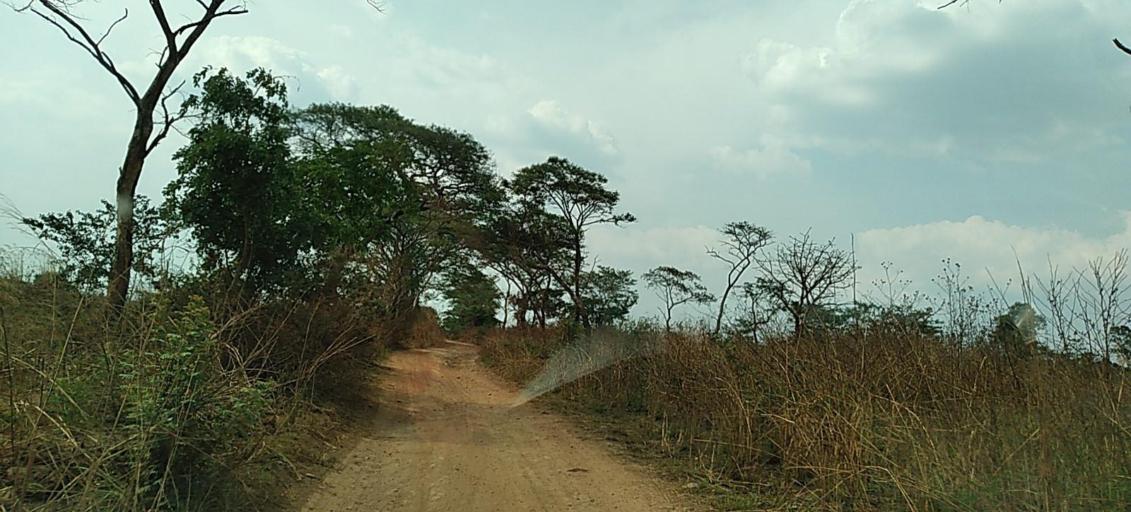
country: ZM
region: Copperbelt
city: Chililabombwe
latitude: -12.3962
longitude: 27.8041
